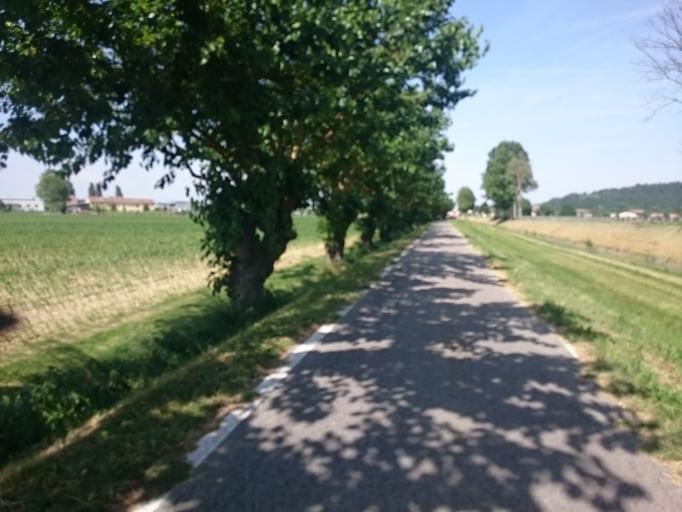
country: IT
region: Veneto
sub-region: Provincia di Padova
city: Bastia
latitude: 45.3779
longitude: 11.6431
